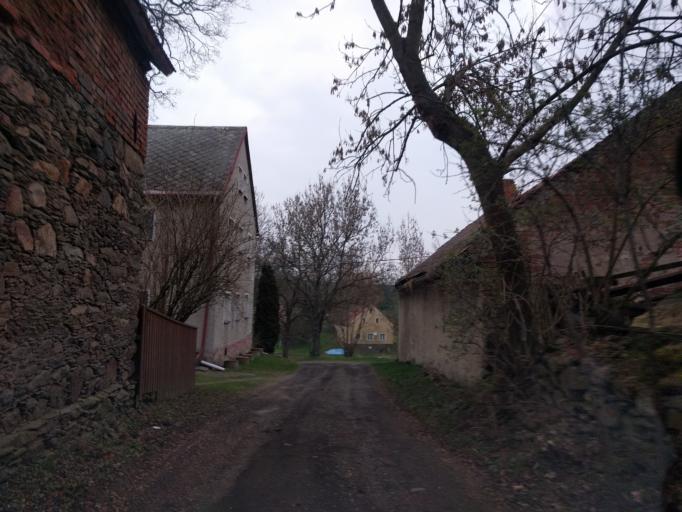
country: CZ
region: Karlovarsky
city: Bochov
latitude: 50.1152
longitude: 13.0894
